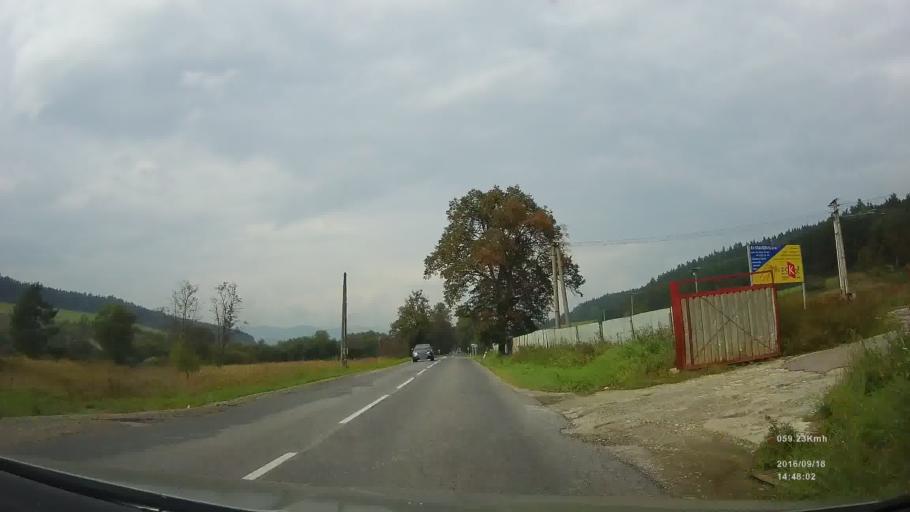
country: SK
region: Kosicky
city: Spisska Nova Ves
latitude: 48.9714
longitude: 20.5823
